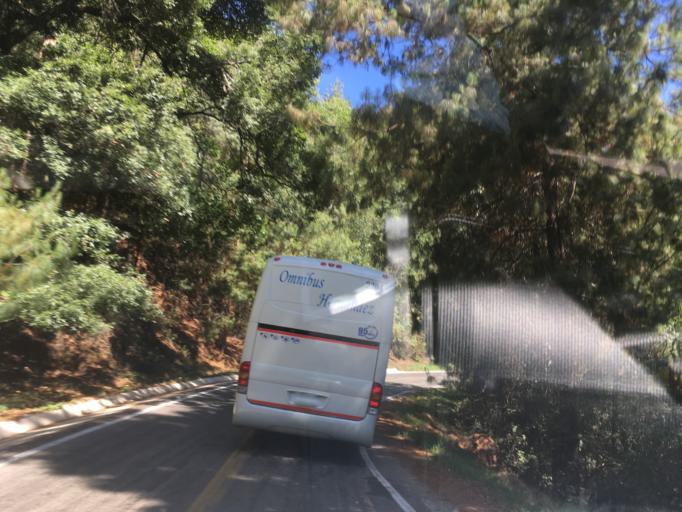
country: MX
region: Michoacan
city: Tzitzio
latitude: 19.6812
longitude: -100.8898
